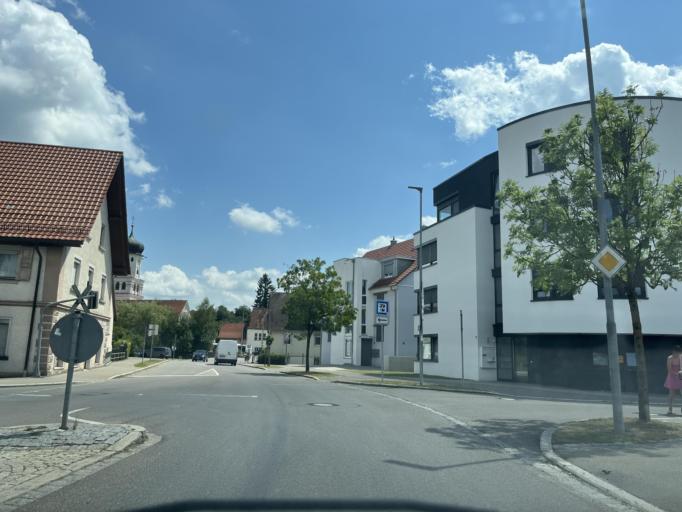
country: DE
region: Baden-Wuerttemberg
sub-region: Tuebingen Region
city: Messkirch
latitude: 47.9934
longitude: 9.1147
